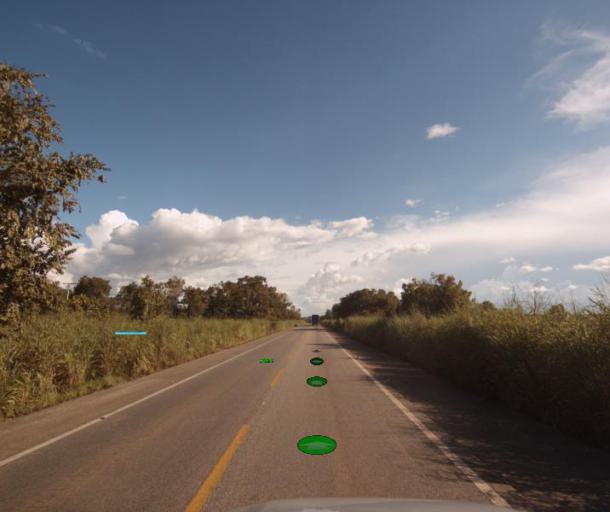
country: BR
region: Goias
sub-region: Porangatu
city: Porangatu
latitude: -13.0840
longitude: -49.1912
